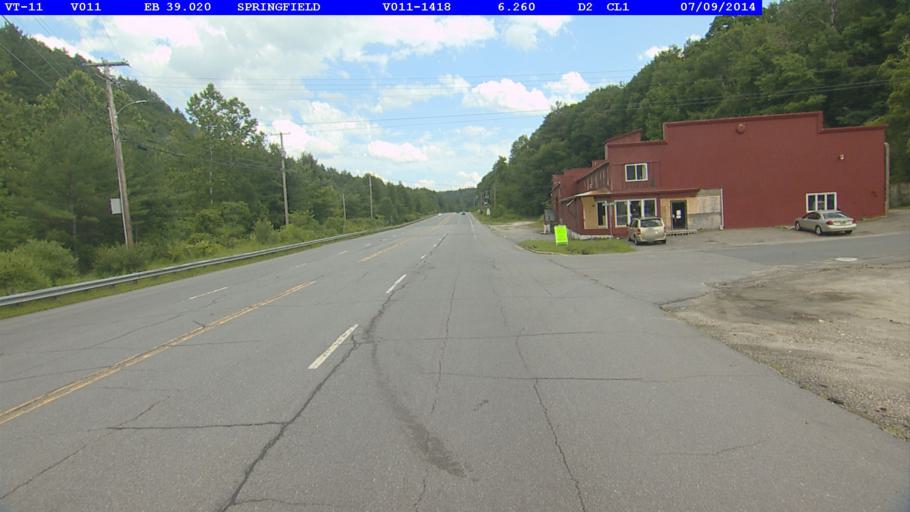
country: US
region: Vermont
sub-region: Windsor County
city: Springfield
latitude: 43.2791
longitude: -72.4675
